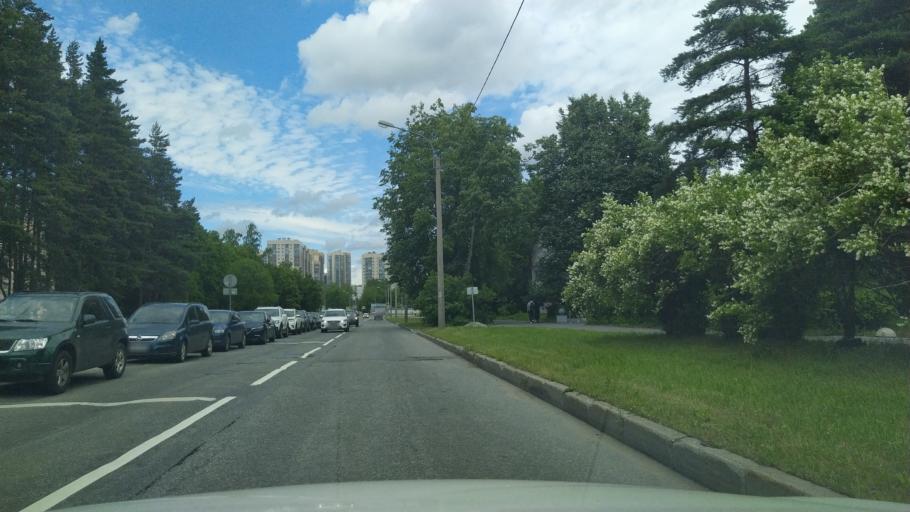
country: RU
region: Leningrad
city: Kalininskiy
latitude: 60.0055
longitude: 30.3842
